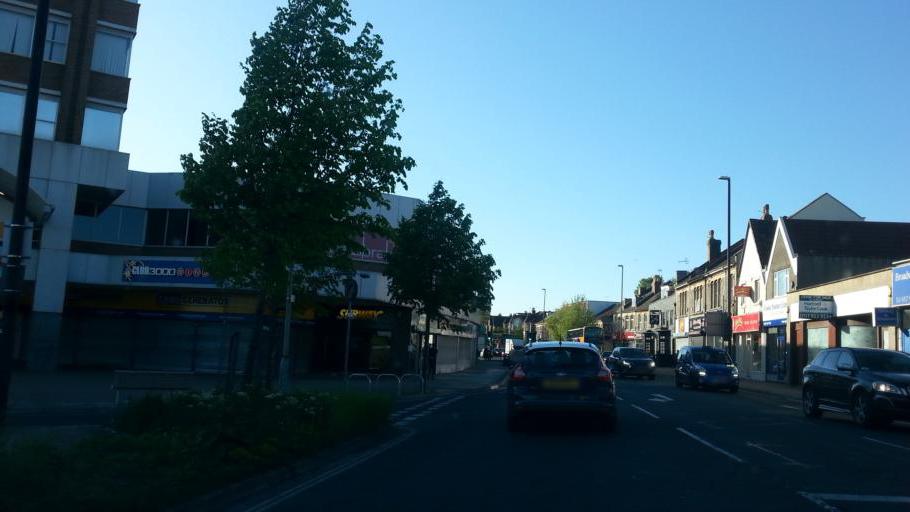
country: GB
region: England
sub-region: Bath and North East Somerset
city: Whitchurch
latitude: 51.4341
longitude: -2.5664
